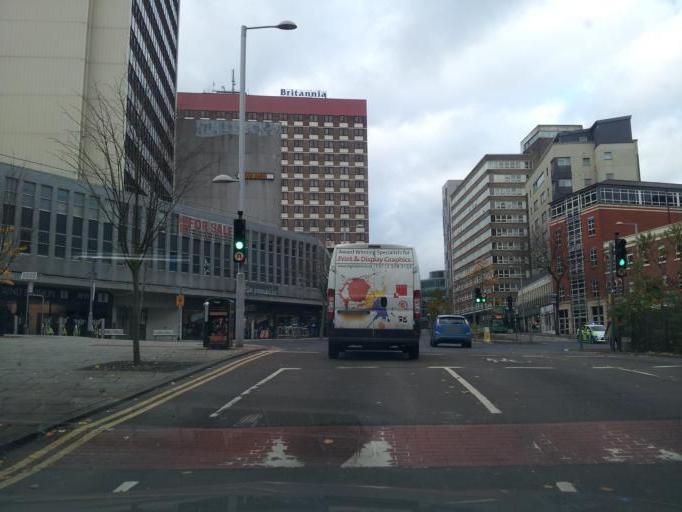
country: GB
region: England
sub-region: Nottingham
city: Nottingham
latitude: 52.9515
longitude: -1.1524
